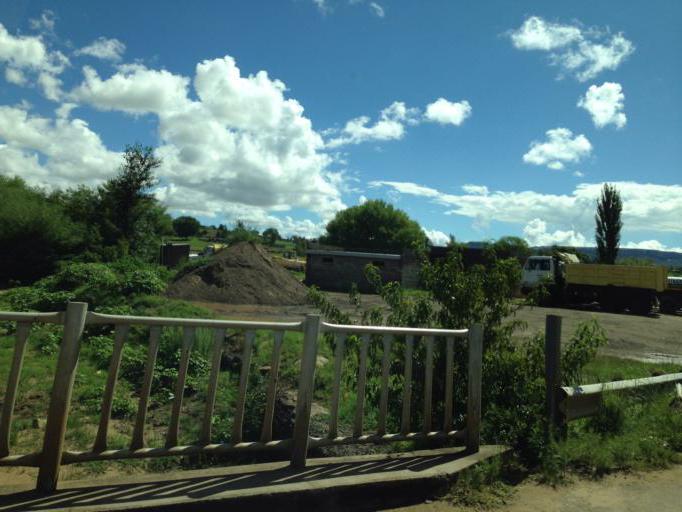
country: LS
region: Mafeteng
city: Mafeteng
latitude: -29.6947
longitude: 27.4451
